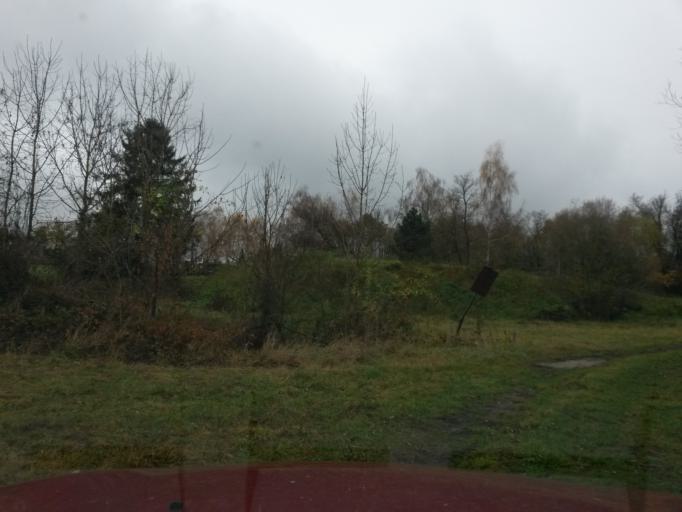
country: SK
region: Kosicky
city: Cierna nad Tisou
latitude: 48.5573
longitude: 21.9510
